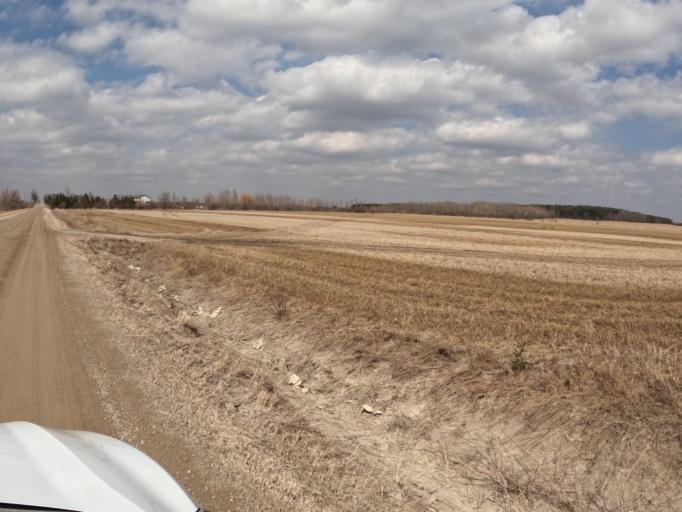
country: CA
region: Ontario
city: Shelburne
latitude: 43.9784
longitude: -80.2688
